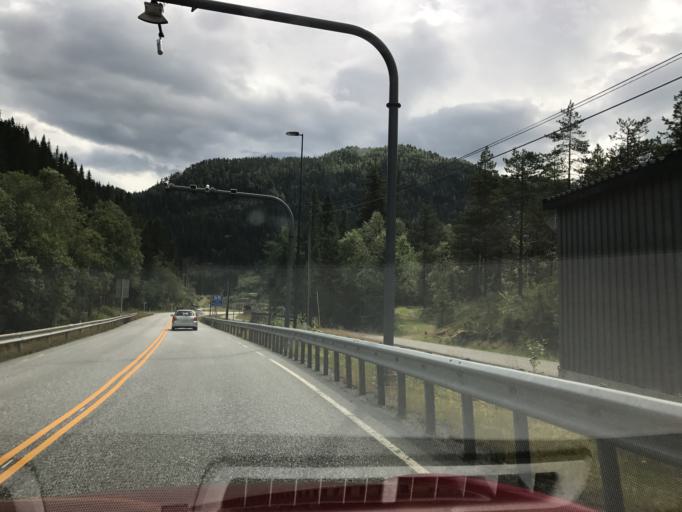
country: NO
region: Hordaland
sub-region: Granvin
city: Granvin
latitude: 60.5881
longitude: 6.6048
